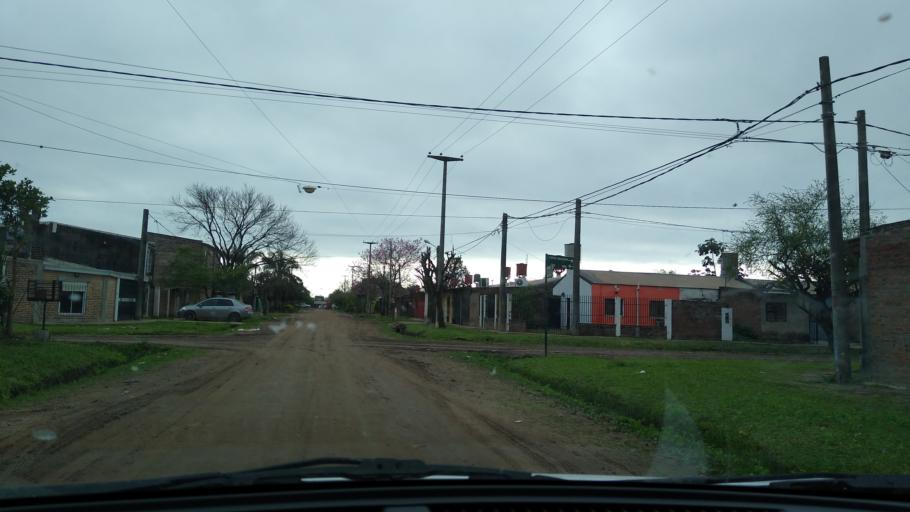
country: AR
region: Chaco
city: Resistencia
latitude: -27.4885
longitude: -58.9782
